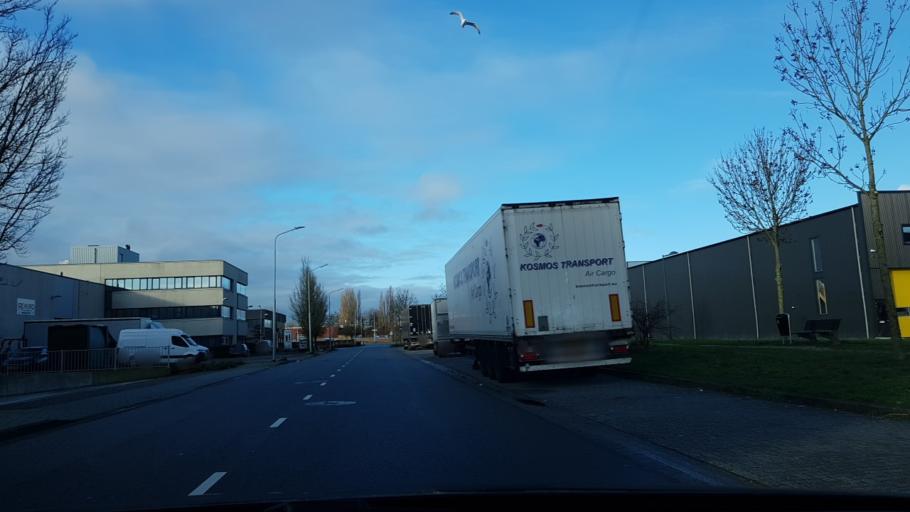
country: NL
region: North Holland
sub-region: Gemeente Haarlemmermeer
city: Hoofddorp
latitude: 52.2936
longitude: 4.7196
